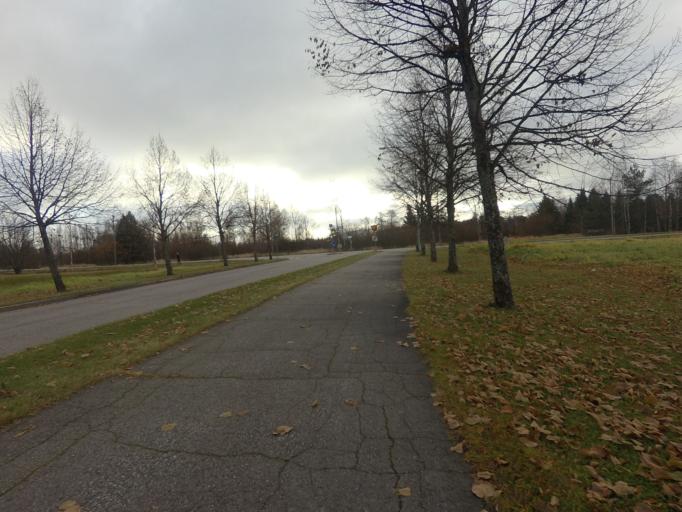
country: FI
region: Uusimaa
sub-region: Helsinki
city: Kauniainen
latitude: 60.1749
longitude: 24.6981
